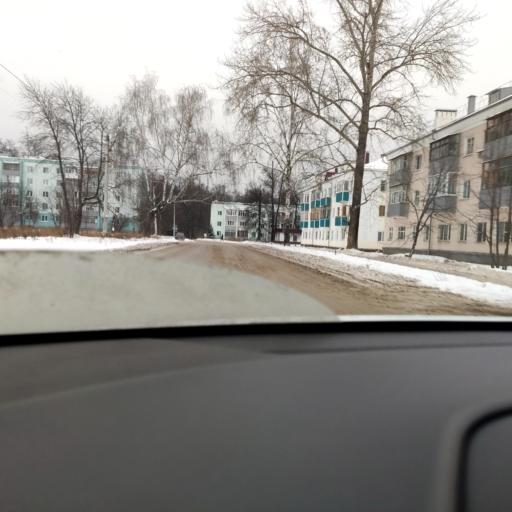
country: RU
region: Tatarstan
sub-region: Zelenodol'skiy Rayon
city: Zelenodolsk
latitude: 55.8546
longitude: 48.4888
